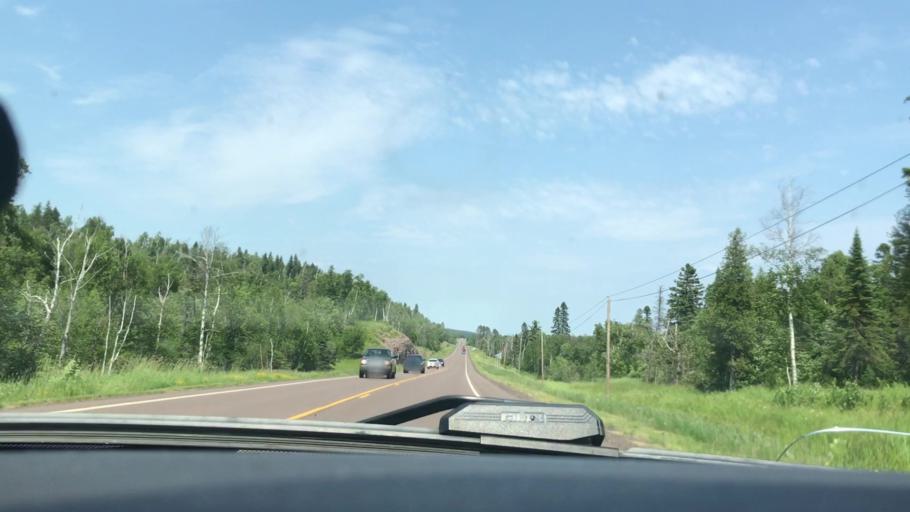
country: US
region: Minnesota
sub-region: Lake County
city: Silver Bay
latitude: 47.4334
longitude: -91.0833
